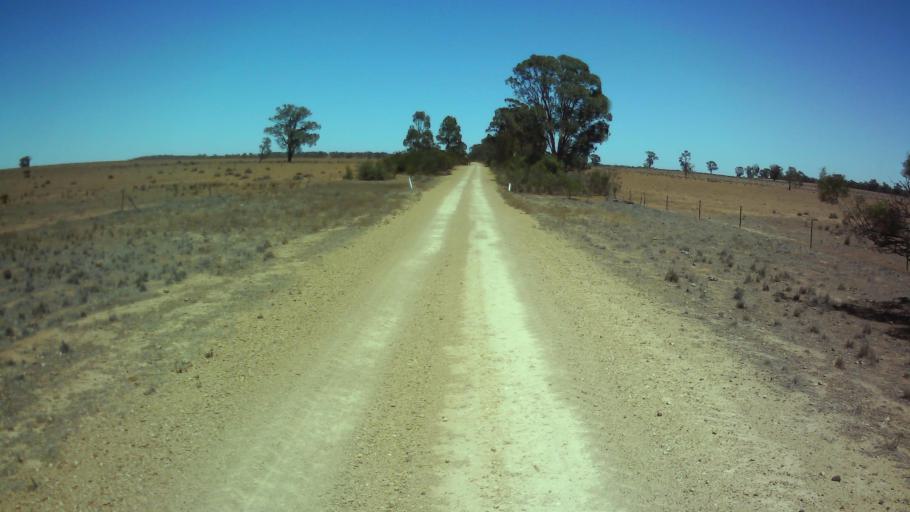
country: AU
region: New South Wales
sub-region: Forbes
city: Forbes
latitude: -33.6942
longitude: 147.8265
